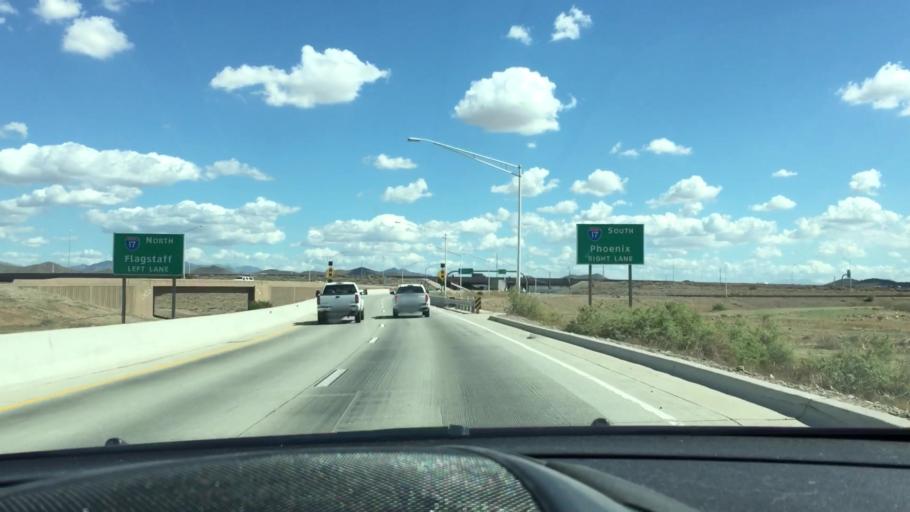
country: US
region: Arizona
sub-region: Maricopa County
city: Anthem
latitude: 33.7702
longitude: -112.1384
